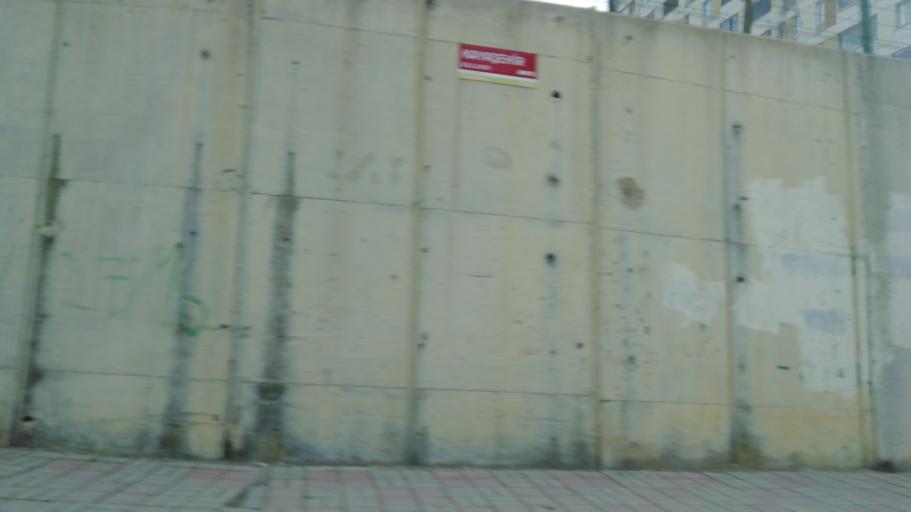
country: TR
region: Istanbul
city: Basaksehir
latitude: 41.1288
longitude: 28.7791
